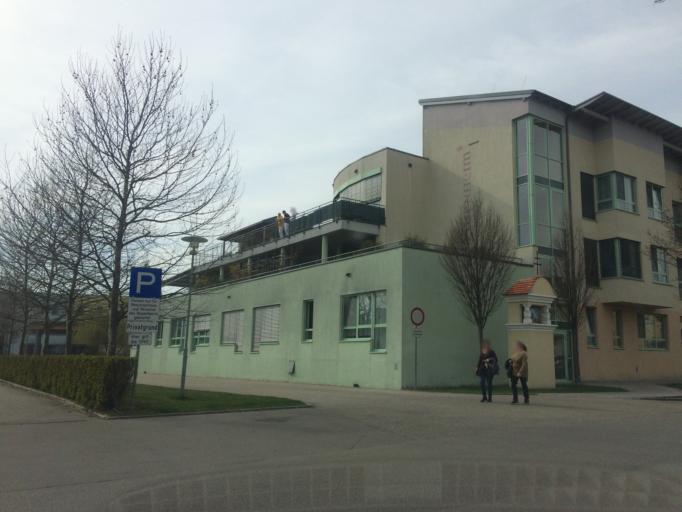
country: AT
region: Lower Austria
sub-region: Politischer Bezirk Tulln
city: Tulln
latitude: 48.3202
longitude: 16.0621
